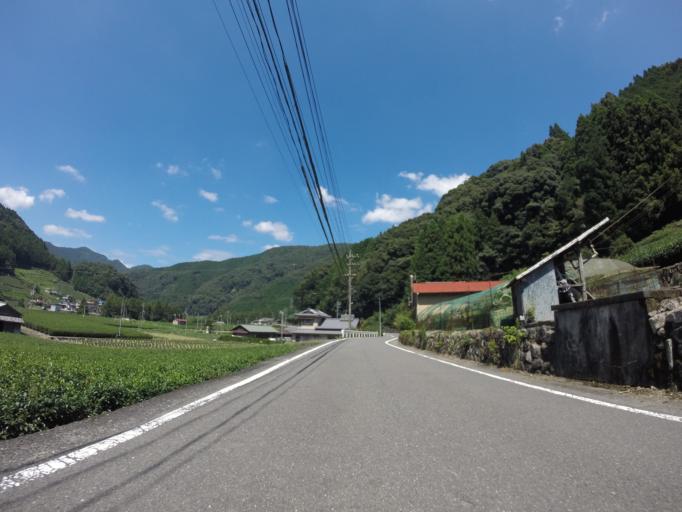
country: JP
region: Shizuoka
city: Shizuoka-shi
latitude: 35.0433
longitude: 138.2510
